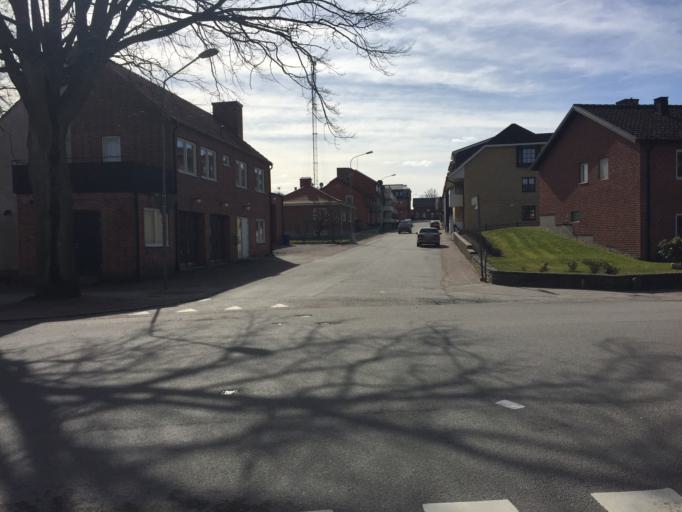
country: SE
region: Skane
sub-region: Sjobo Kommun
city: Sjoebo
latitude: 55.6337
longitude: 13.7025
